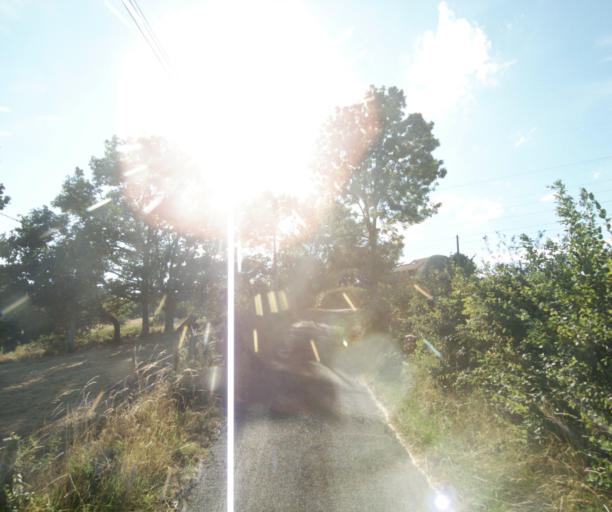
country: FR
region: Rhone-Alpes
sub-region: Departement du Rhone
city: Lentilly
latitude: 45.8032
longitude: 4.6823
